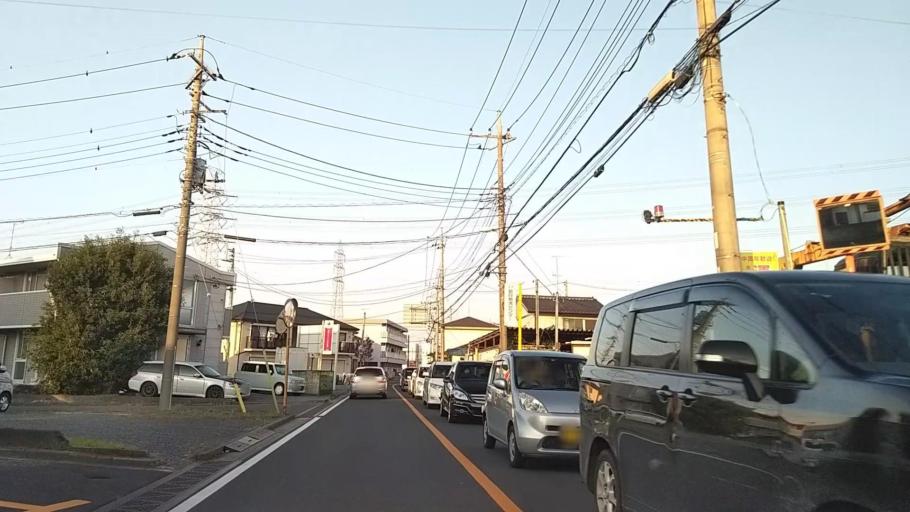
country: JP
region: Saitama
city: Sayama
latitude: 35.8693
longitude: 139.4227
